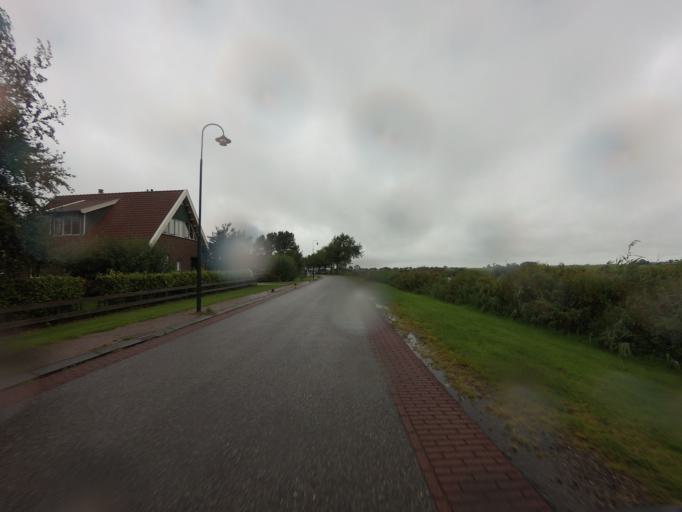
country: NL
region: Friesland
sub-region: Sudwest Fryslan
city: Workum
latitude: 53.0108
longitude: 5.4765
